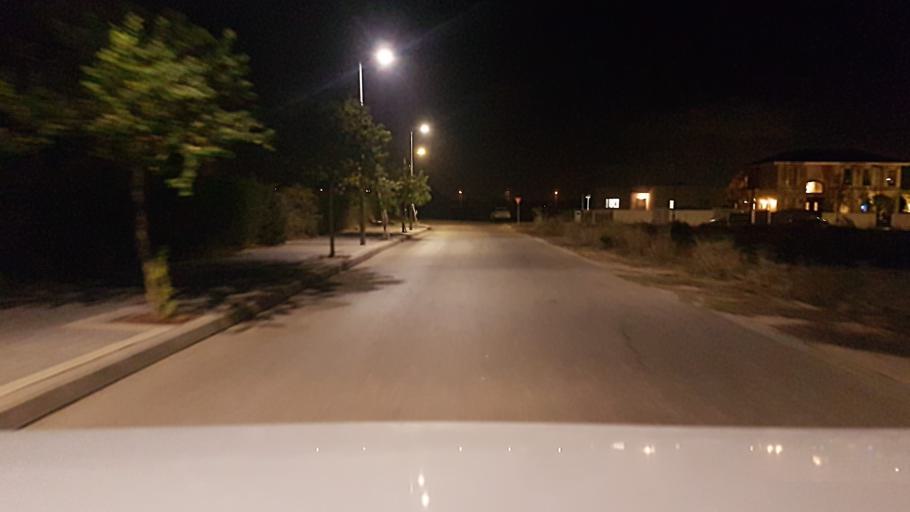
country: IL
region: Central District
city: Nehalim
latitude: 32.0739
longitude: 34.9237
